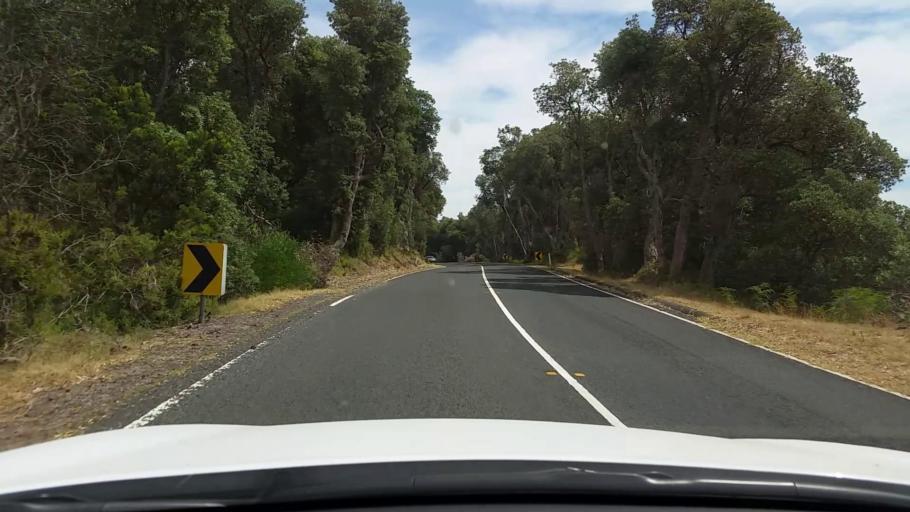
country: AU
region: Victoria
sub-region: Mornington Peninsula
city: Saint Andrews Beach
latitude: -38.4749
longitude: 144.9296
